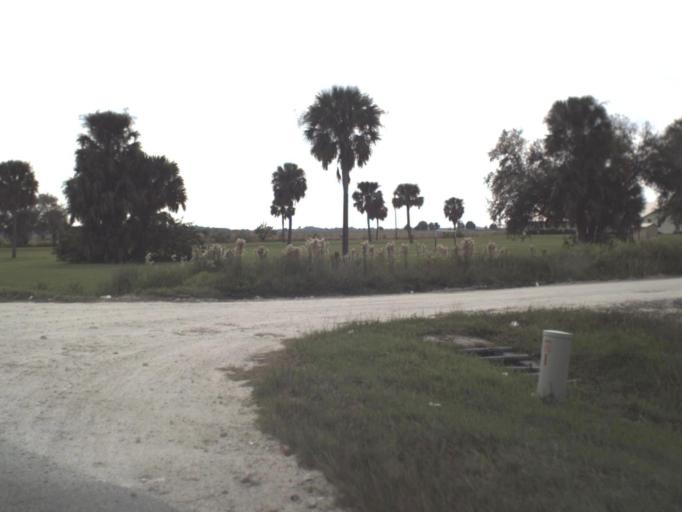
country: US
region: Florida
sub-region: Okeechobee County
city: Cypress Quarters
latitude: 27.4133
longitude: -80.8138
